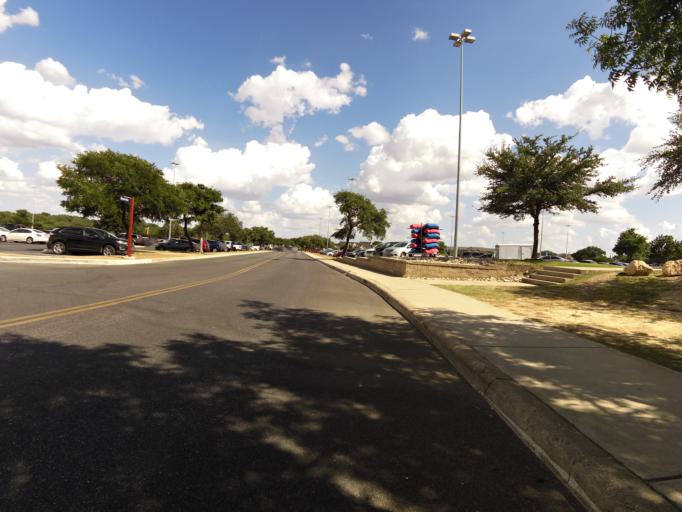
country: US
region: Texas
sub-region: Bexar County
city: Helotes
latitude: 29.5813
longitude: -98.6220
